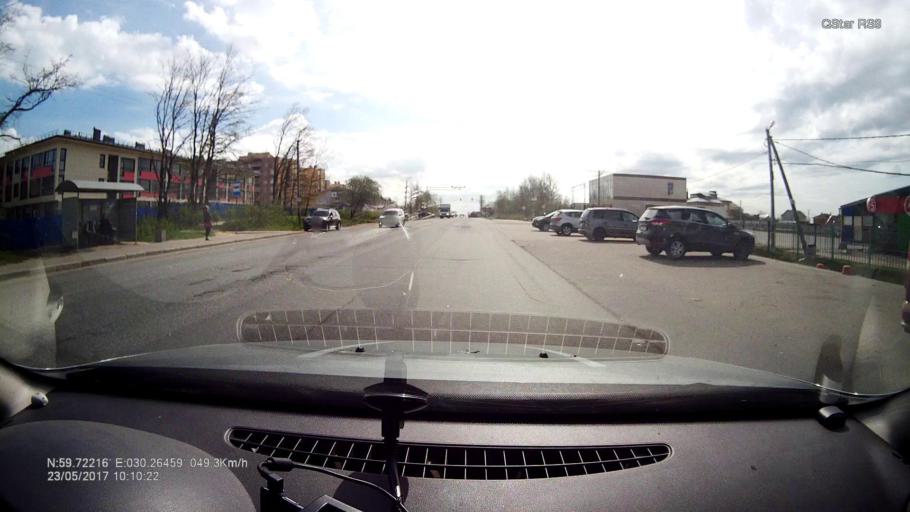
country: RU
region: St.-Petersburg
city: Aleksandrovskaya
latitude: 59.7221
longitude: 30.2648
